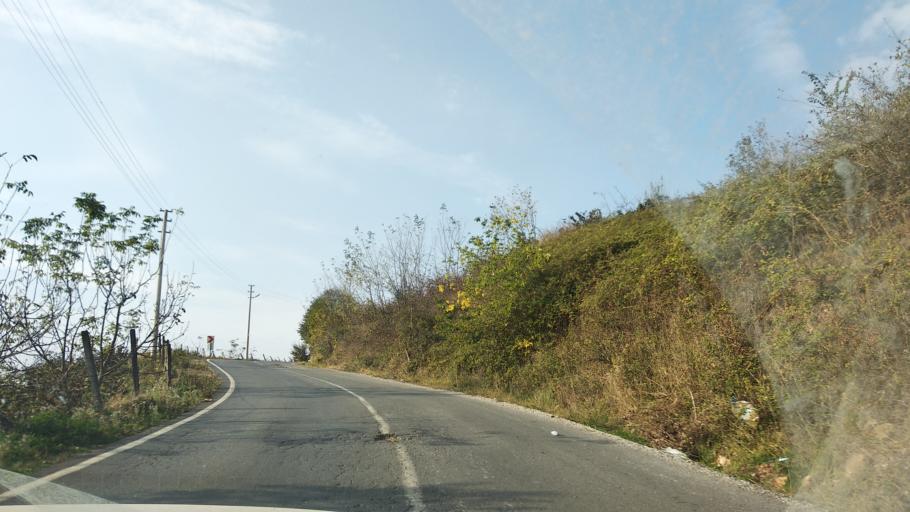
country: TR
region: Sakarya
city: Karasu
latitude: 41.0608
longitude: 30.6192
